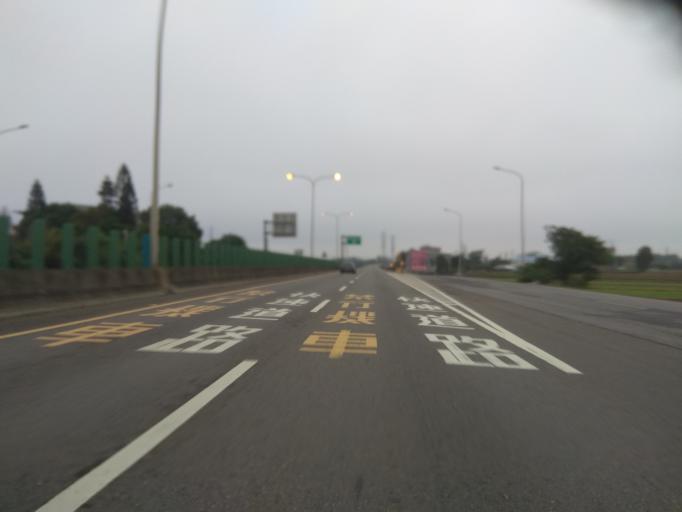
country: TW
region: Taiwan
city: Taoyuan City
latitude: 24.9868
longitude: 121.1245
